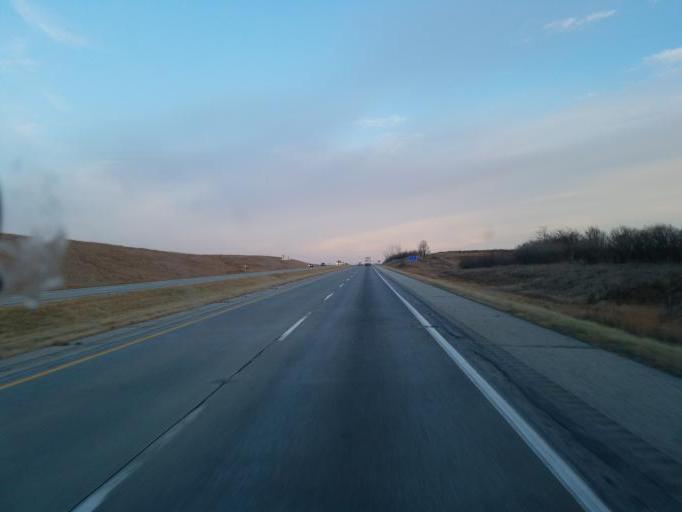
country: US
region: Iowa
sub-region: Pottawattamie County
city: Avoca
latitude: 41.5002
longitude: -95.5168
